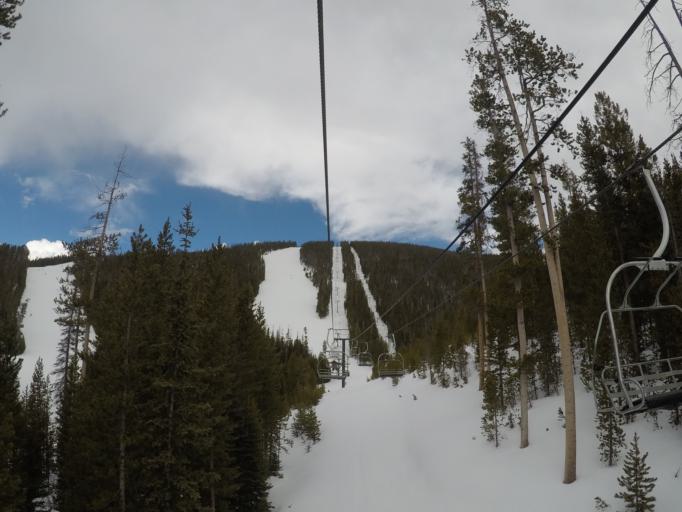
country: US
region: Montana
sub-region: Granite County
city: Philipsburg
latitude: 46.2532
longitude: -113.2422
